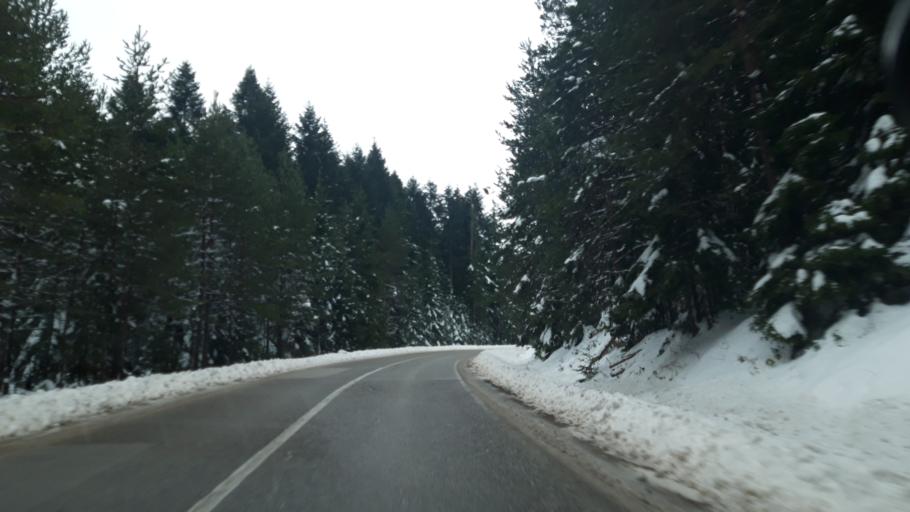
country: BA
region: Republika Srpska
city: Han Pijesak
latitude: 44.0496
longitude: 18.9303
